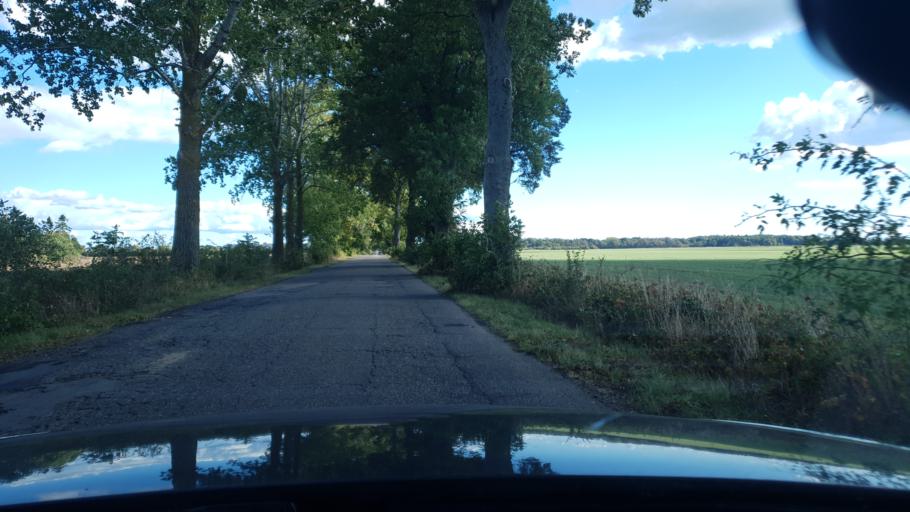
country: PL
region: Pomeranian Voivodeship
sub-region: Powiat pucki
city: Zelistrzewo
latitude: 54.6877
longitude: 18.4377
